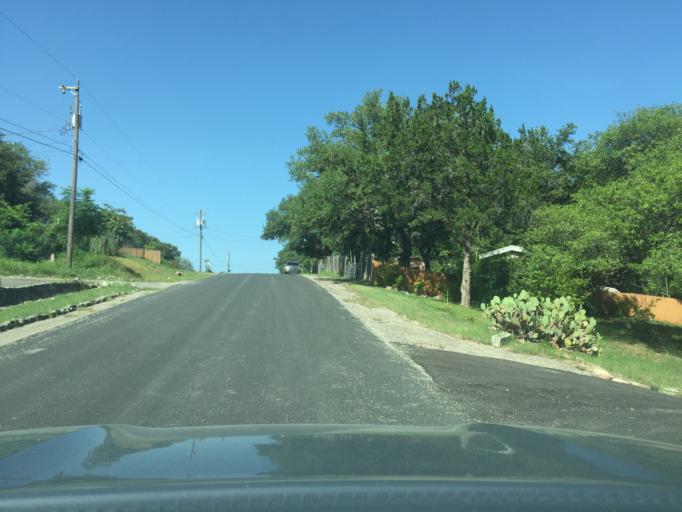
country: US
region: Texas
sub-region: Bexar County
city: Timberwood Park
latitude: 29.7075
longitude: -98.4725
